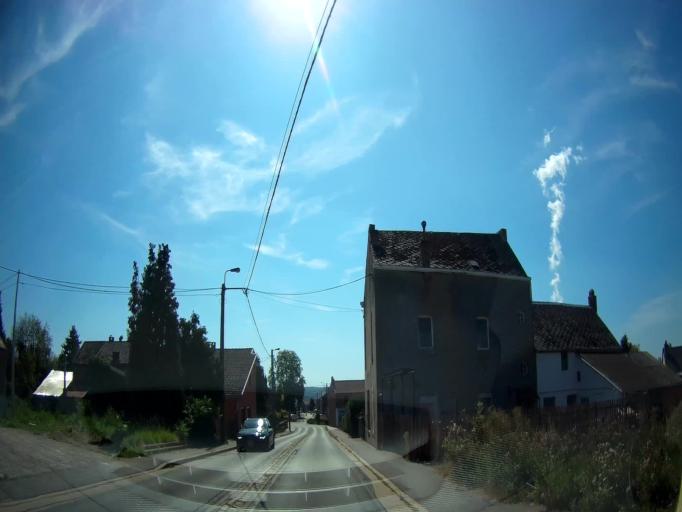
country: BE
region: Wallonia
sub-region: Province de Liege
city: Amay
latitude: 50.5546
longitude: 5.3065
